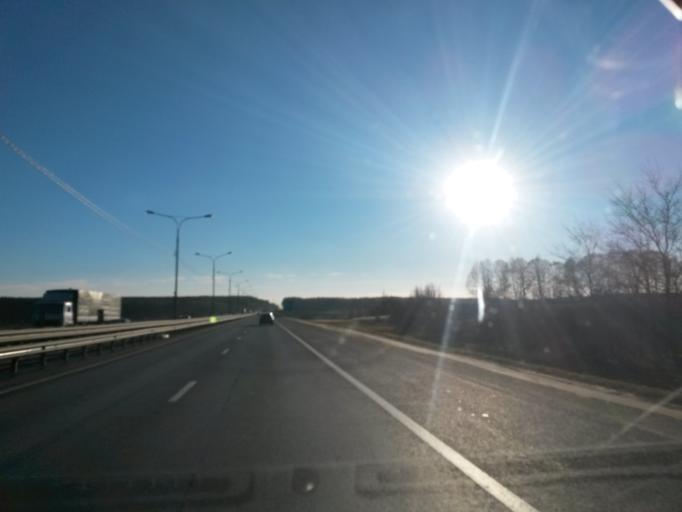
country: RU
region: Moskovskaya
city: Kostino
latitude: 56.0495
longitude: 37.8960
